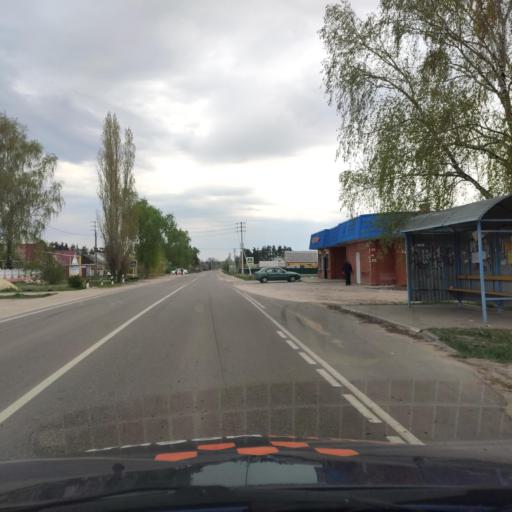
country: RU
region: Voronezj
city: Podgornoye
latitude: 51.8789
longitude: 39.1730
